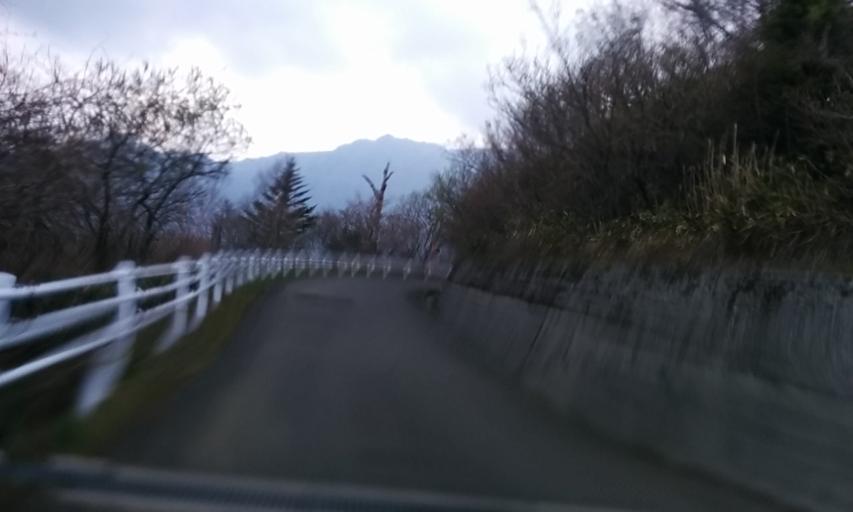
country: JP
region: Ehime
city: Saijo
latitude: 33.7828
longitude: 133.2155
